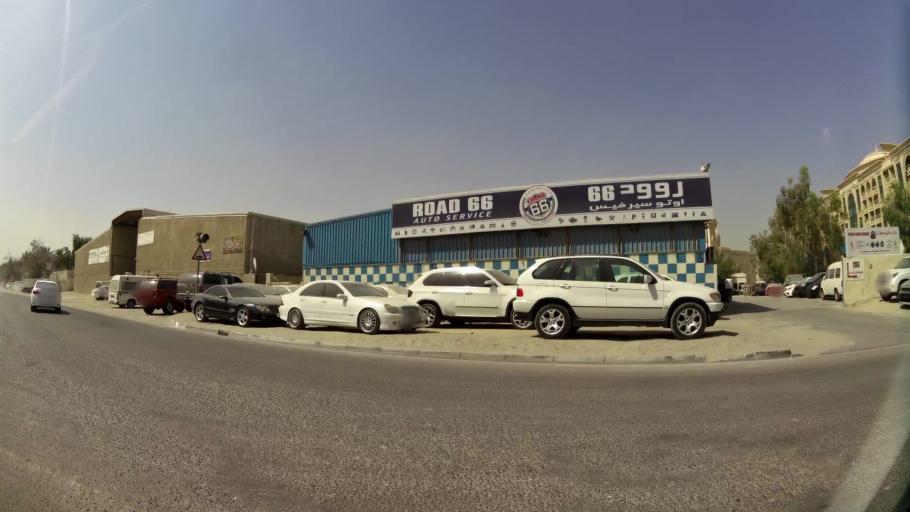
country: AE
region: Ash Shariqah
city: Sharjah
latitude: 25.2825
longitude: 55.3908
